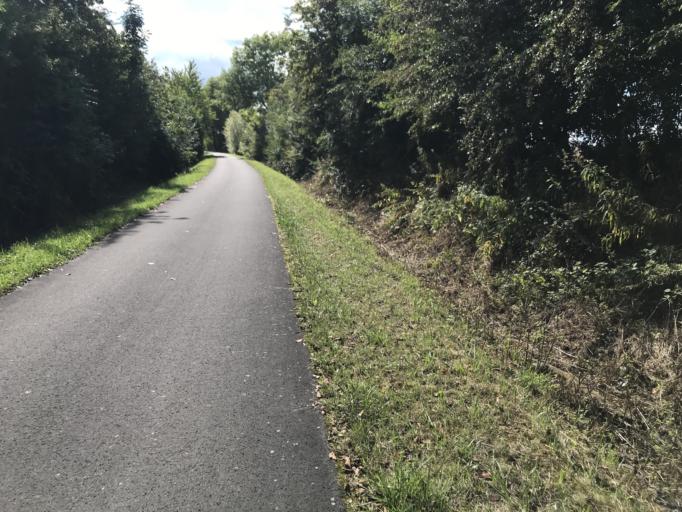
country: DE
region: Hesse
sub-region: Regierungsbezirk Kassel
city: Sachsenhausen
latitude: 51.2619
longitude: 8.9881
